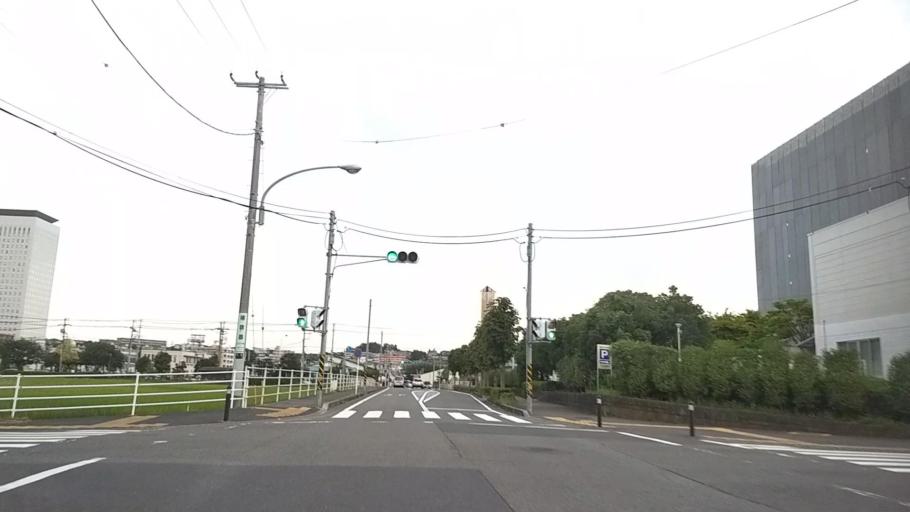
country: JP
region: Kanagawa
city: Atsugi
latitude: 35.4470
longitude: 139.3900
